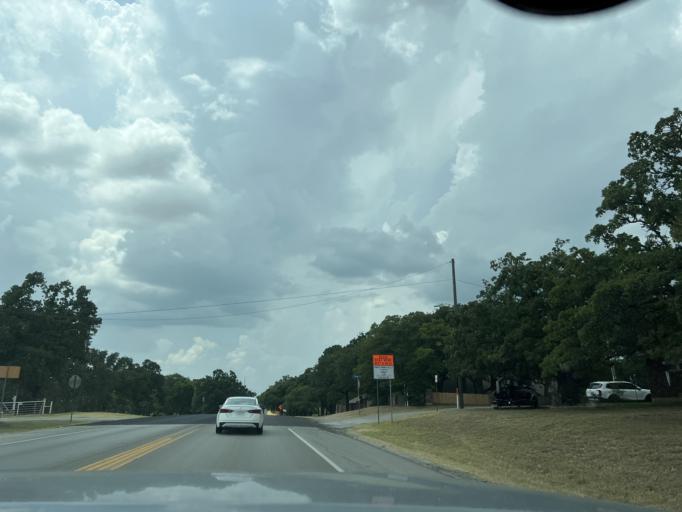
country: US
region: Texas
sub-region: Wise County
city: Decatur
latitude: 33.2039
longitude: -97.6027
